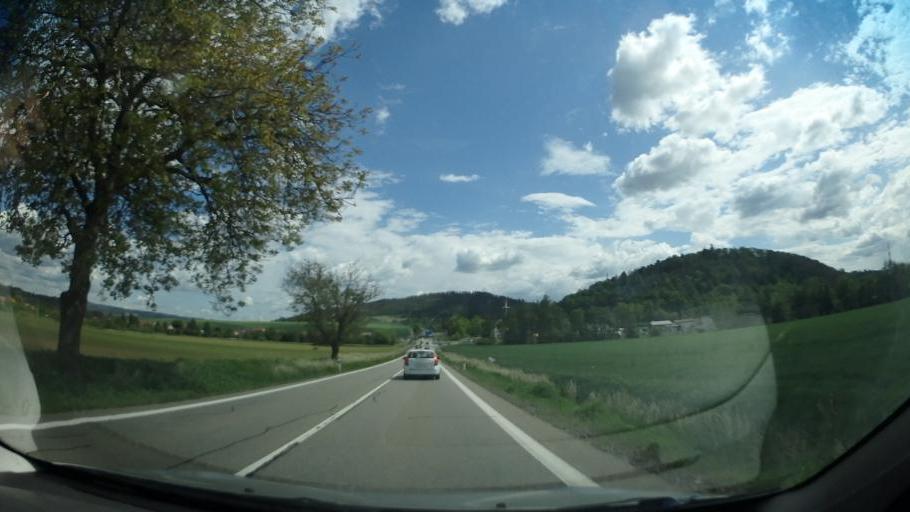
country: CZ
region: South Moravian
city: Boritov
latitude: 49.4225
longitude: 16.5835
